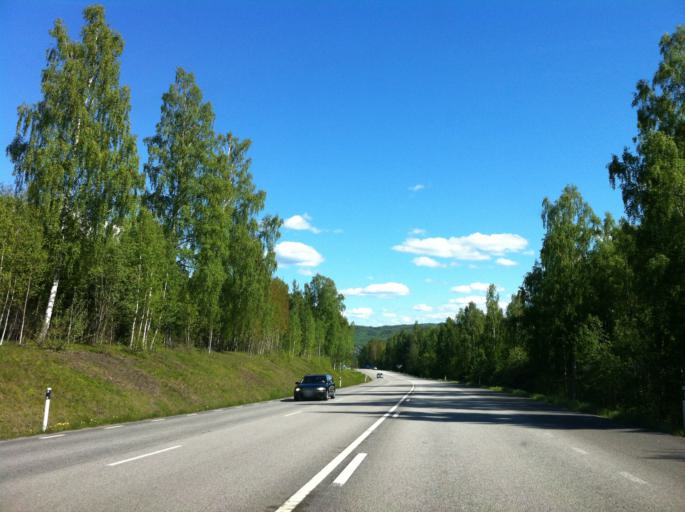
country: SE
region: Dalarna
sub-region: Rattviks Kommun
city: Raettvik
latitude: 60.8988
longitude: 15.0852
